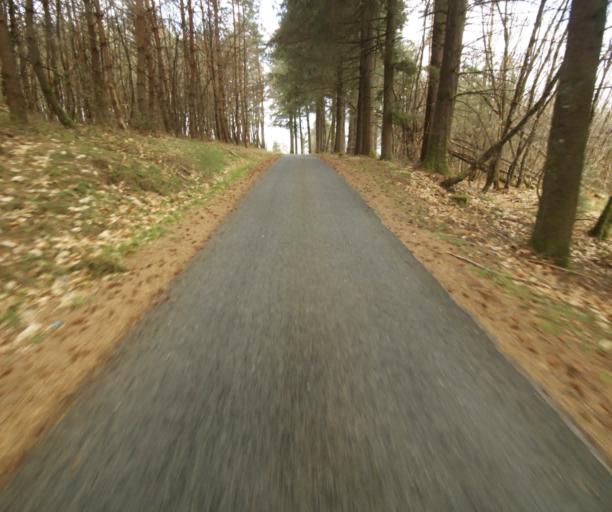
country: FR
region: Limousin
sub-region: Departement de la Correze
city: Correze
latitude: 45.3330
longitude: 1.9381
